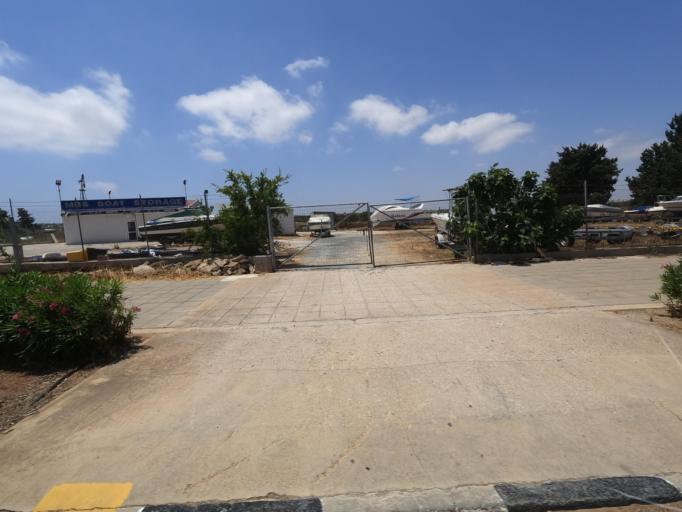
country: CY
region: Ammochostos
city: Paralimni
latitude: 35.0455
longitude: 34.0189
